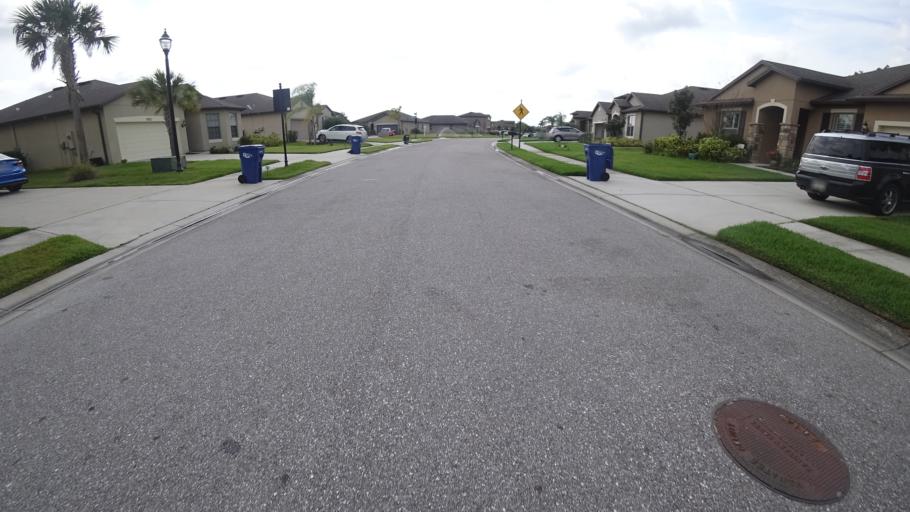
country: US
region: Florida
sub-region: Manatee County
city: Ellenton
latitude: 27.5686
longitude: -82.4675
